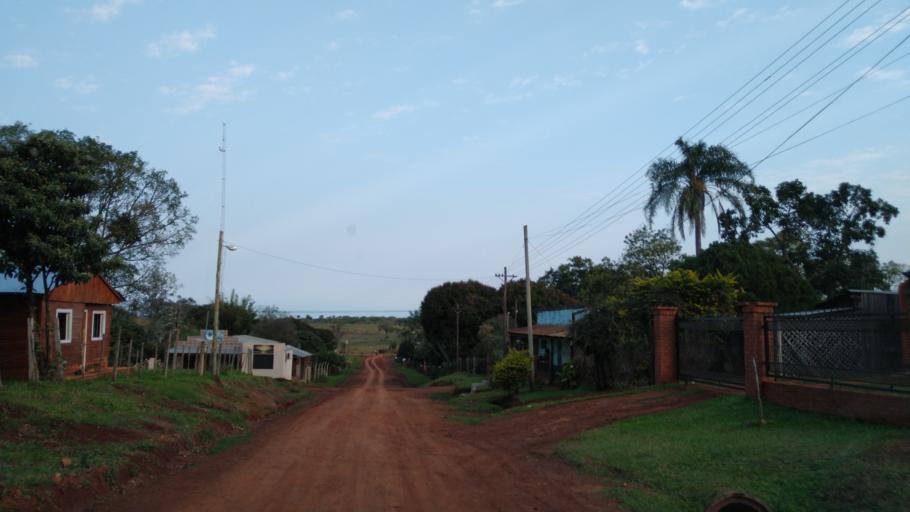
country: AR
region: Corrientes
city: San Carlos
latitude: -27.7502
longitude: -55.9007
